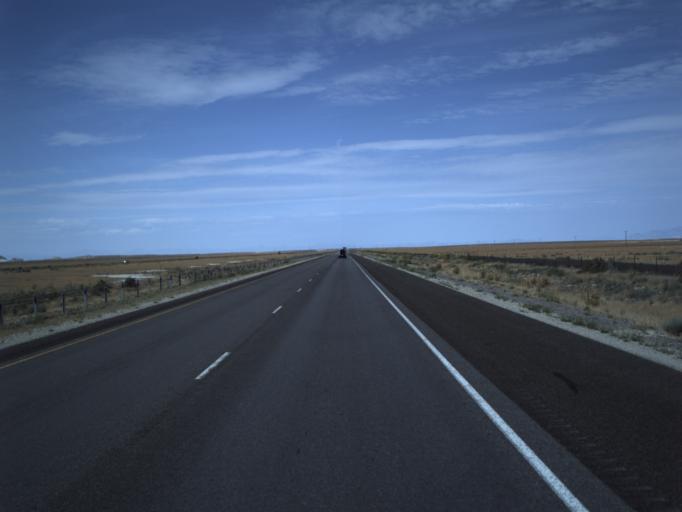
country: US
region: Utah
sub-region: Tooele County
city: Grantsville
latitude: 40.7268
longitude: -113.2126
